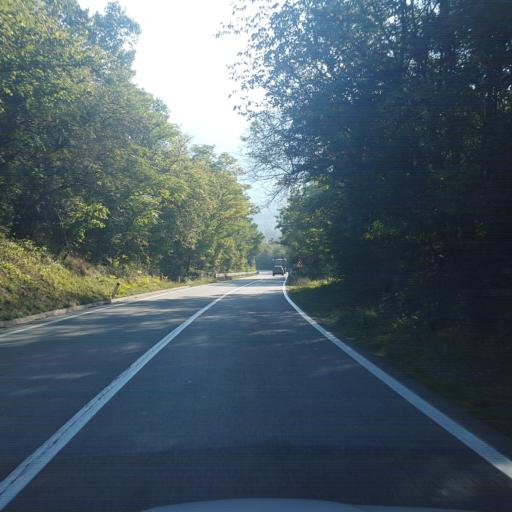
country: RS
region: Central Serbia
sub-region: Nisavski Okrug
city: Svrljig
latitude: 43.3279
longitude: 22.1066
